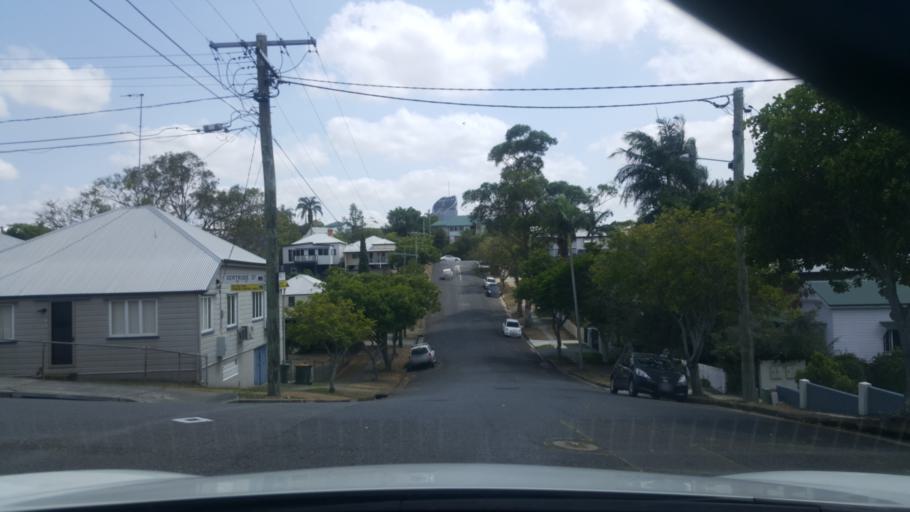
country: AU
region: Queensland
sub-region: Brisbane
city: South Brisbane
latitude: -27.4896
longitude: 153.0229
